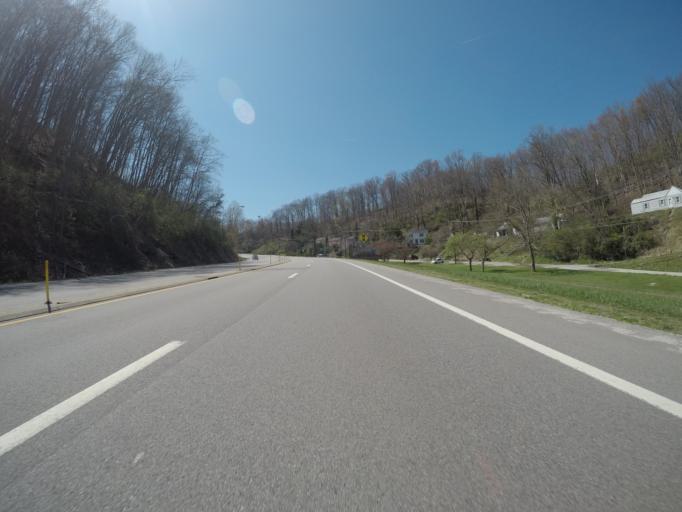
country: US
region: West Virginia
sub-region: Kanawha County
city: Charleston
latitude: 38.3515
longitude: -81.6007
